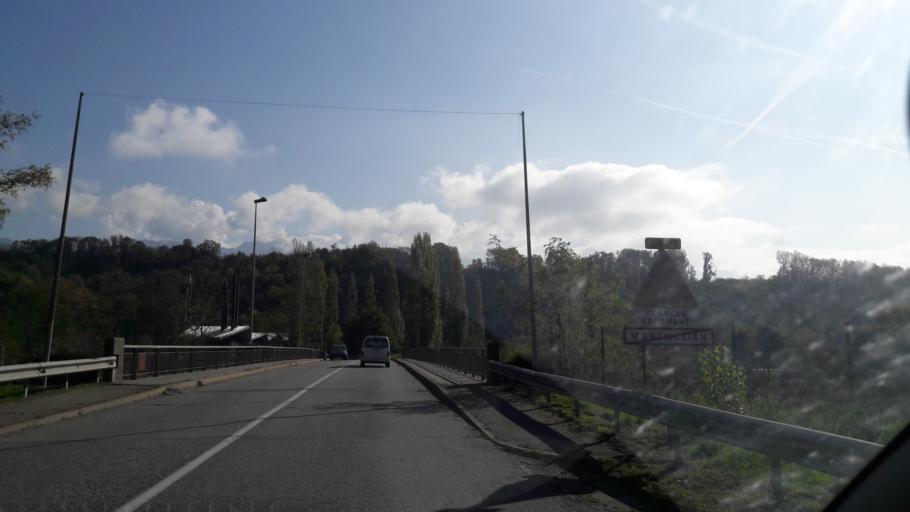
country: FR
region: Rhone-Alpes
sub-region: Departement de la Savoie
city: Montmelian
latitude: 45.4964
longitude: 6.0553
